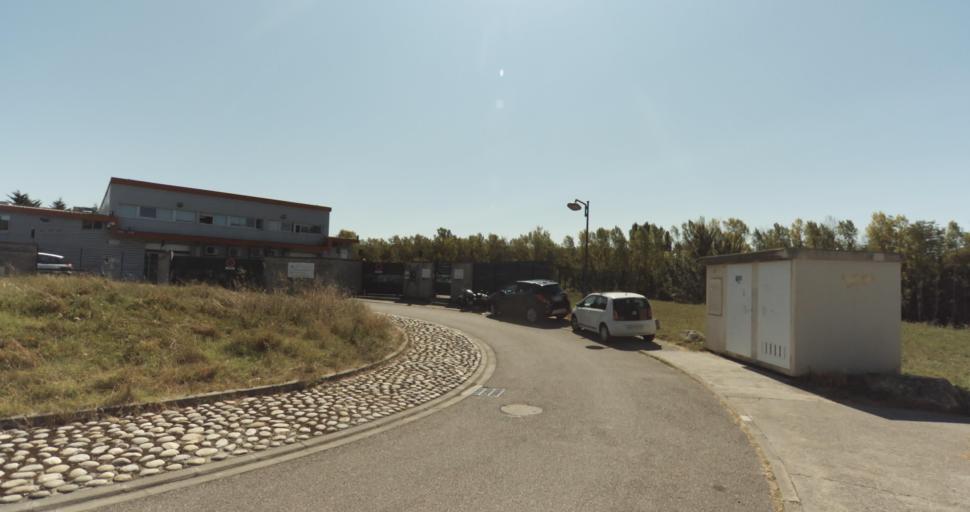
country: FR
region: Midi-Pyrenees
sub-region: Departement de la Haute-Garonne
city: Saint-Jean
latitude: 43.6477
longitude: 1.5018
